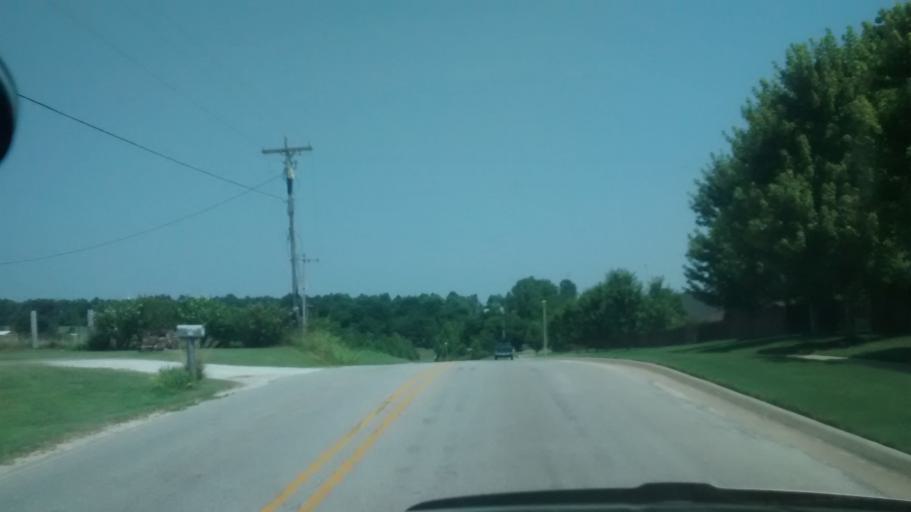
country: US
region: Arkansas
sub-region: Washington County
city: Farmington
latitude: 36.0715
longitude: -94.2533
